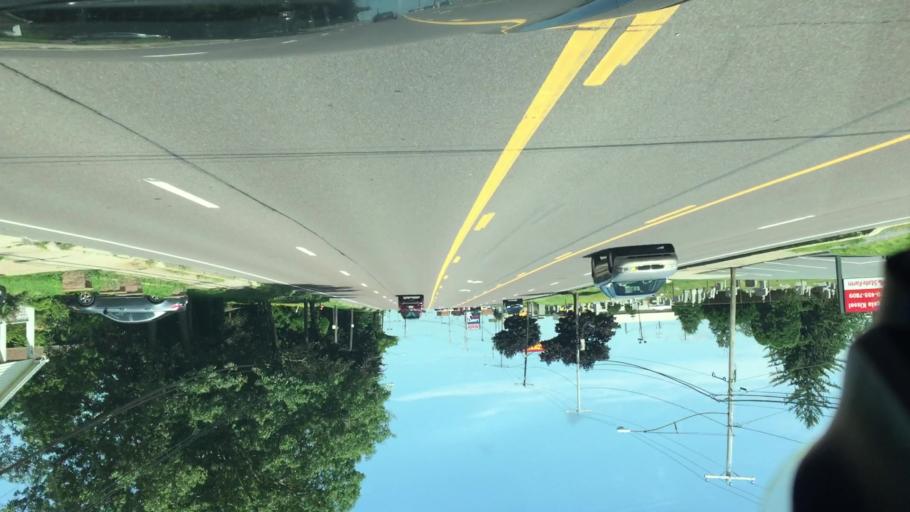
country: US
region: Pennsylvania
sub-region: Luzerne County
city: West Hazleton
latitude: 40.9672
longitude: -76.0001
